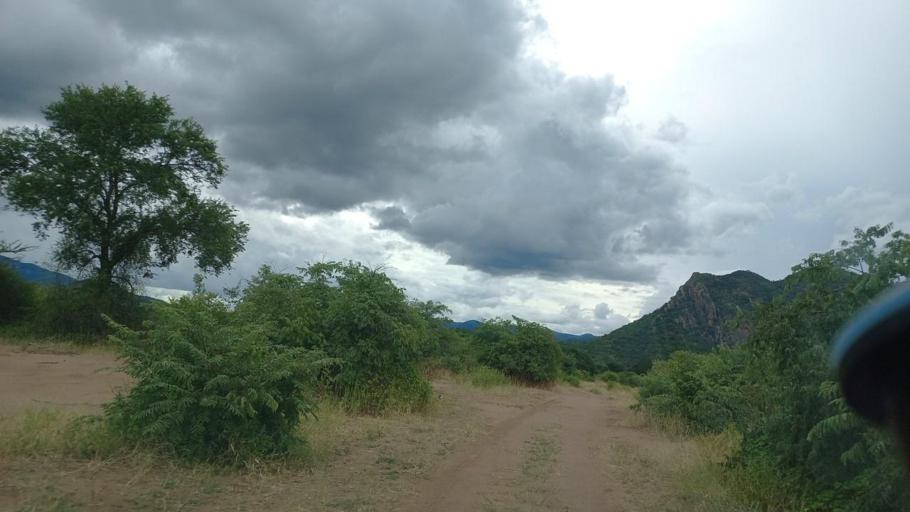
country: ZM
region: Lusaka
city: Luangwa
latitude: -15.6179
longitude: 30.2699
